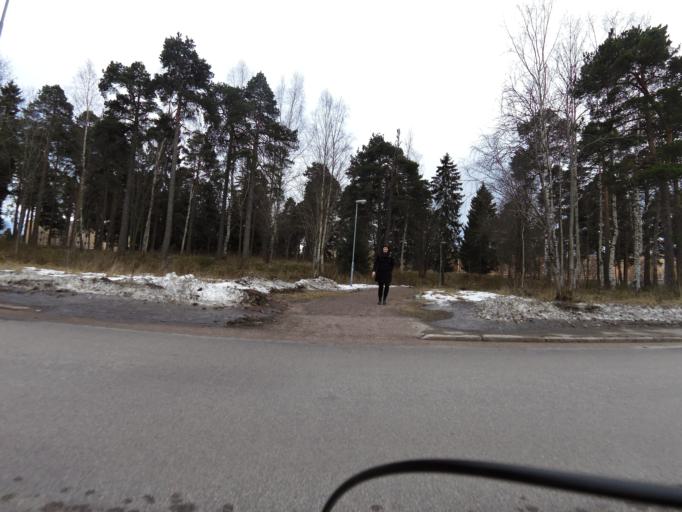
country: SE
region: Gaevleborg
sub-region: Gavle Kommun
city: Gavle
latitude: 60.6617
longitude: 17.1462
